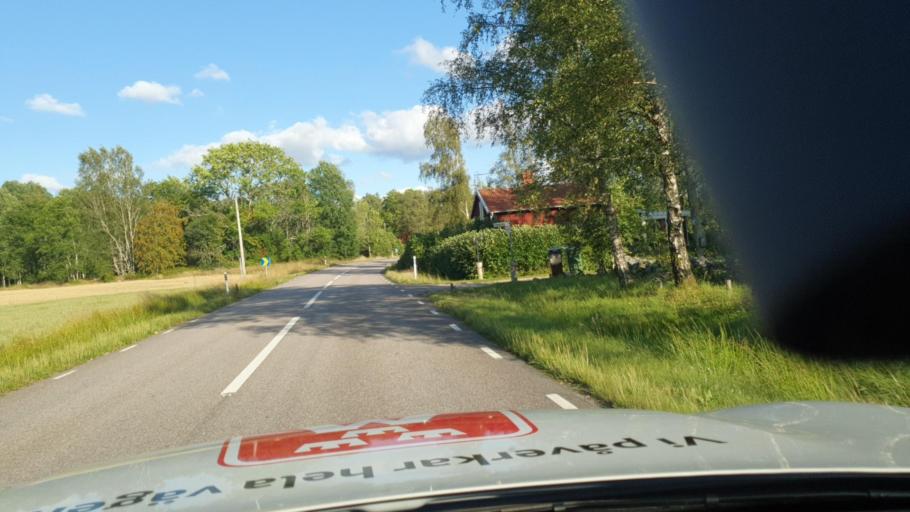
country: SE
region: Vaestra Goetaland
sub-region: Vanersborgs Kommun
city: Vanersborg
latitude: 58.4924
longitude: 12.2519
